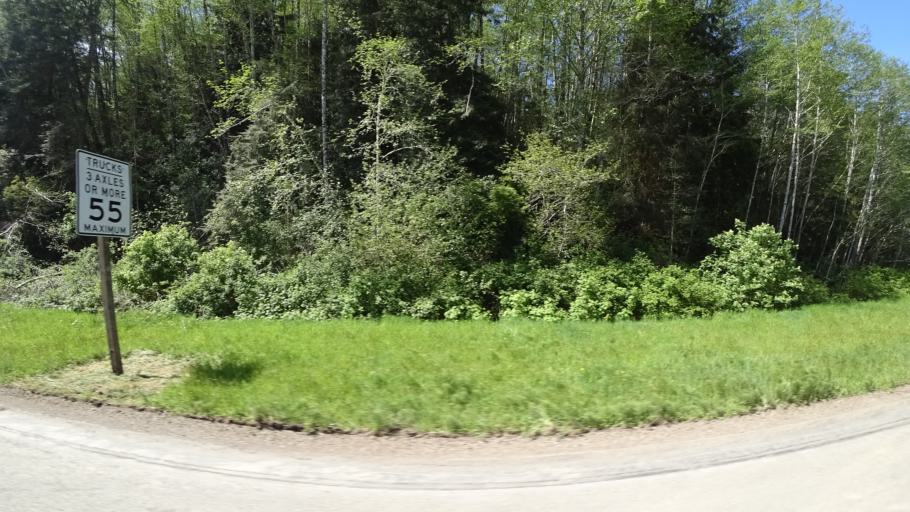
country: US
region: California
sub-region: Del Norte County
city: Bertsch-Oceanview
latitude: 41.4594
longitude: -124.0326
